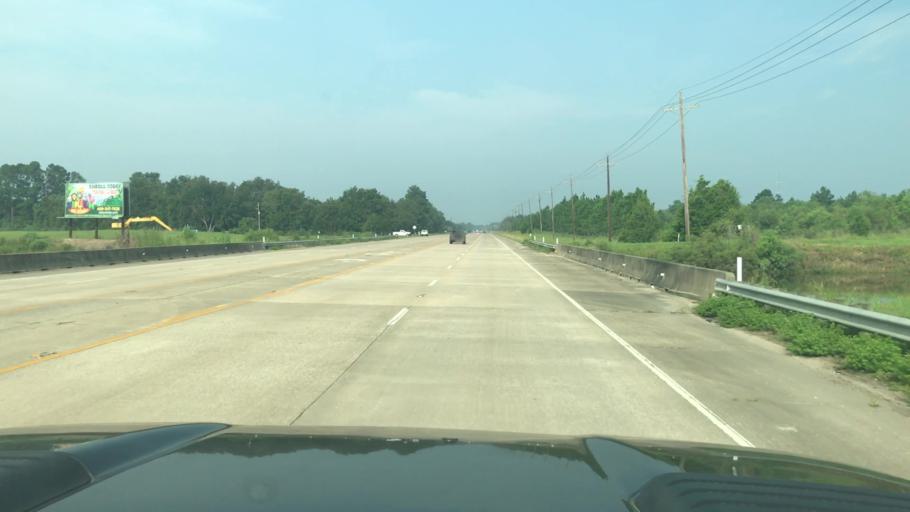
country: US
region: Texas
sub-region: Jefferson County
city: Bevil Oaks
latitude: 30.1331
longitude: -94.2230
